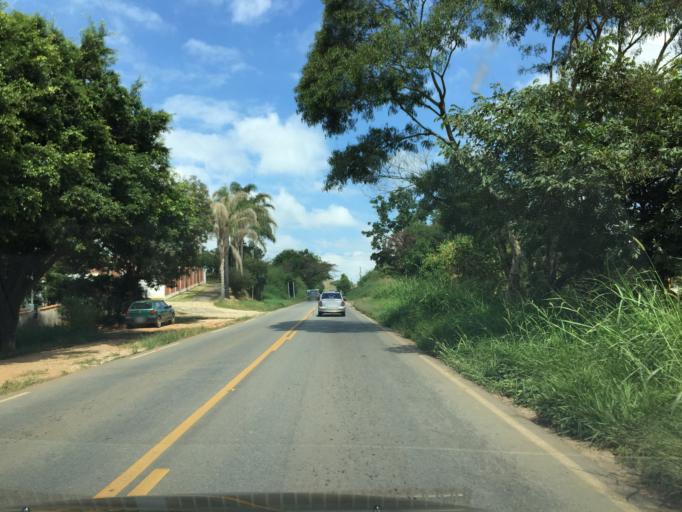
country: BR
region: Minas Gerais
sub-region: Itanhandu
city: Itanhandu
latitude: -22.3117
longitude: -44.9316
